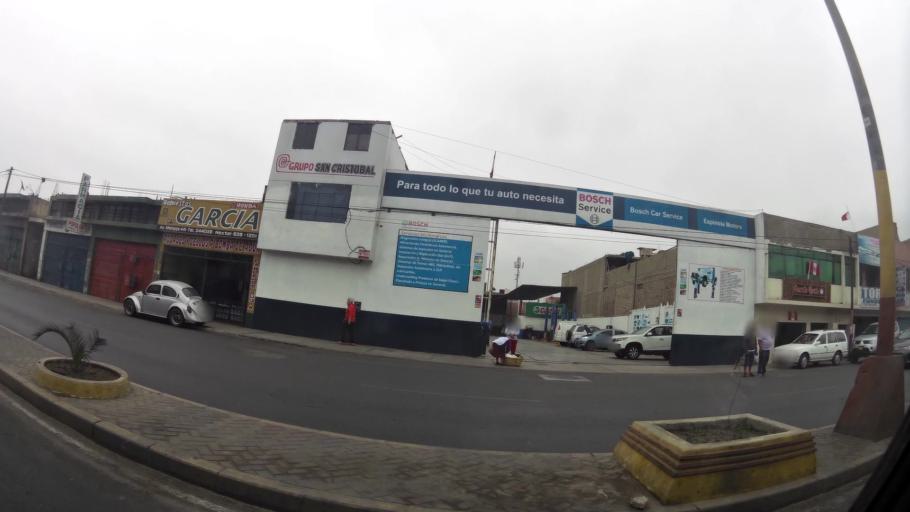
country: PE
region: Ancash
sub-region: Provincia de Santa
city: Chimbote
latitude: -9.0796
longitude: -78.5837
